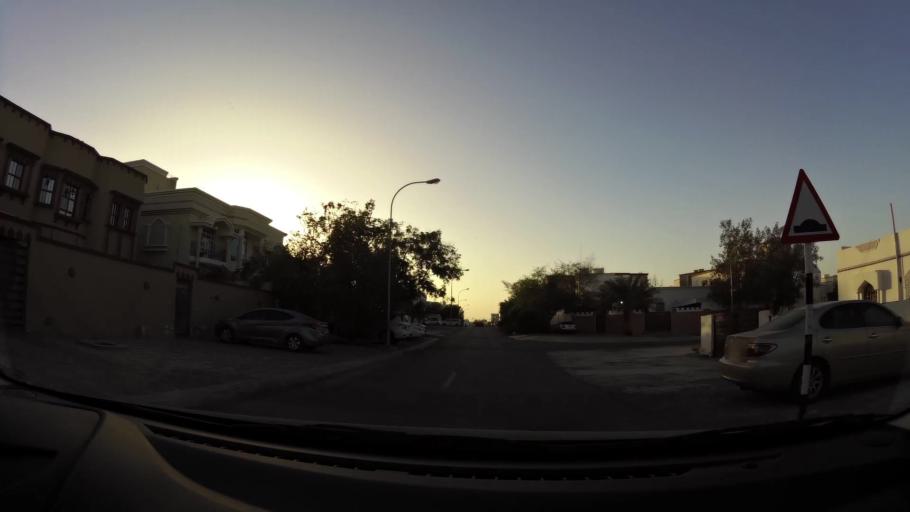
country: OM
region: Muhafazat Masqat
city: As Sib al Jadidah
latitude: 23.6042
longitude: 58.2291
